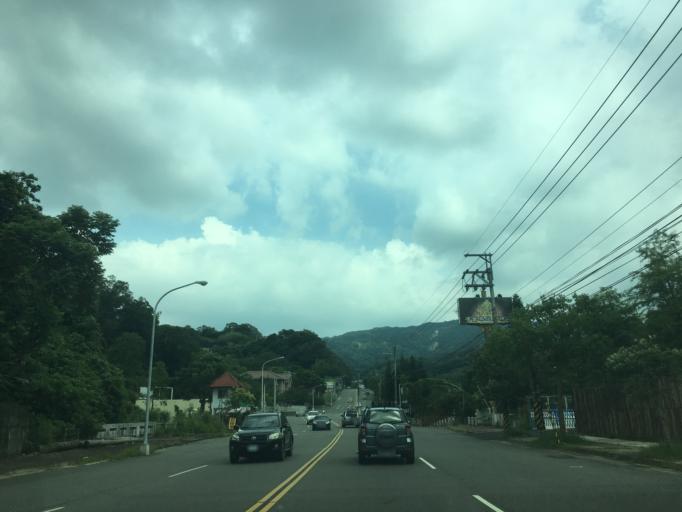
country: TW
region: Taiwan
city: Fengyuan
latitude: 24.1993
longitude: 120.7646
